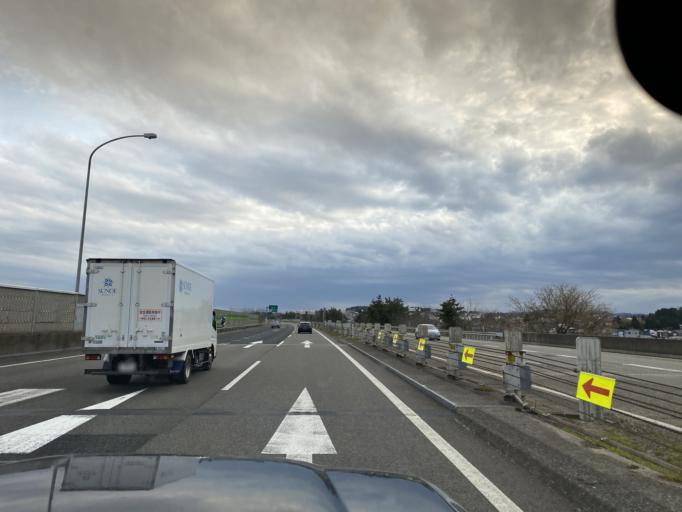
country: JP
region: Niigata
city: Nagaoka
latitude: 37.4560
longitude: 138.7900
